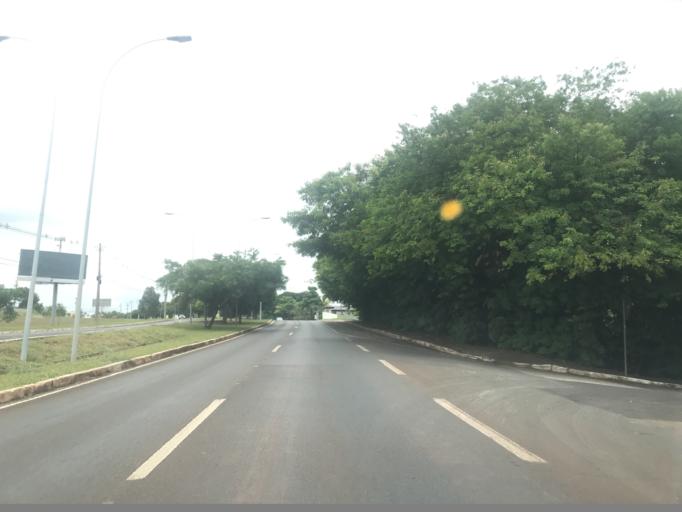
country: BR
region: Federal District
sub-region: Brasilia
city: Brasilia
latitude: -15.8343
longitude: -47.8305
